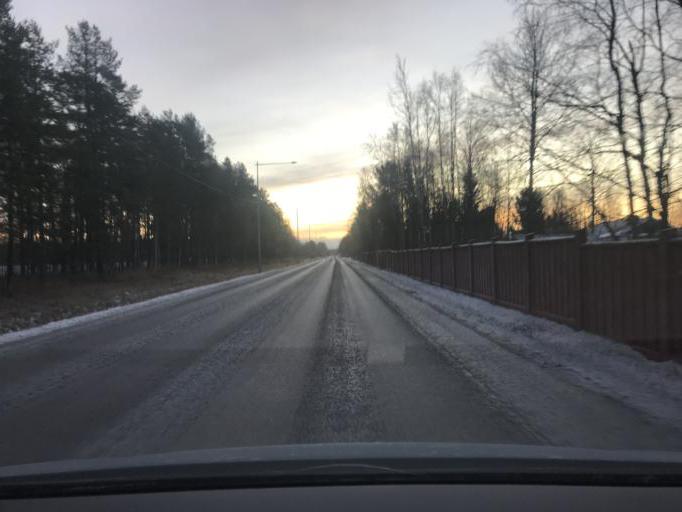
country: SE
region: Norrbotten
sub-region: Lulea Kommun
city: Gammelstad
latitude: 65.6486
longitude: 21.9955
